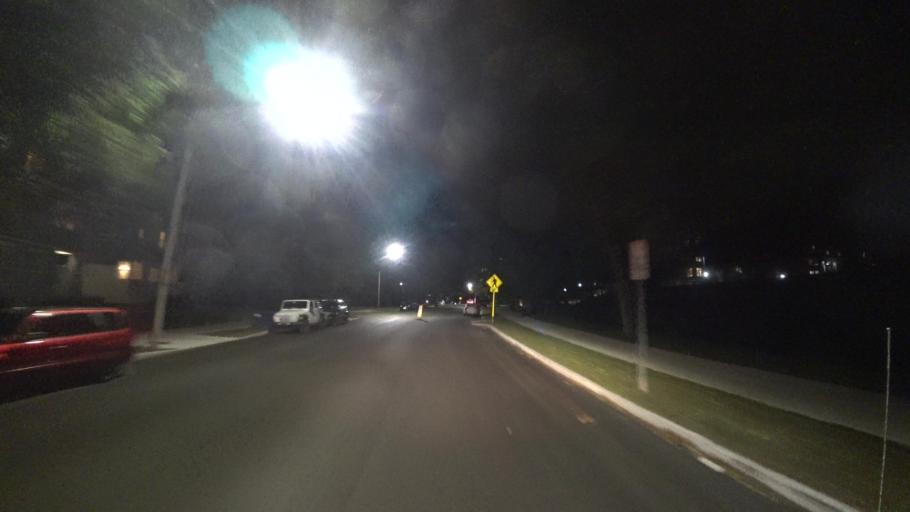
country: US
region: Massachusetts
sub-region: Middlesex County
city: Medford
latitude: 42.4026
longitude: -71.1203
